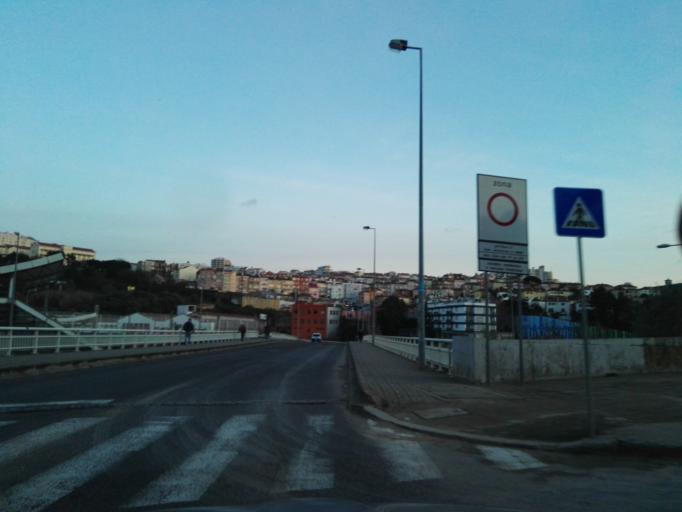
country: PT
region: Lisbon
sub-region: Lisbon
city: Lisbon
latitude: 38.7323
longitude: -9.1693
